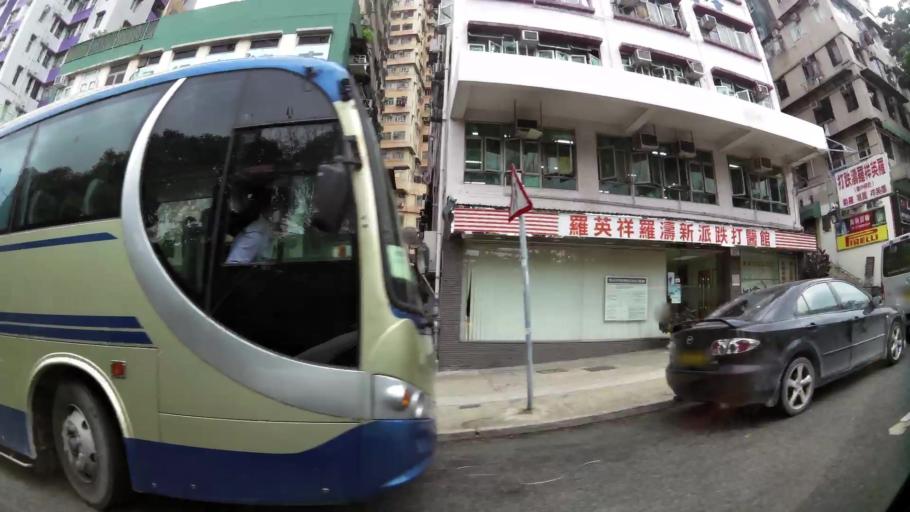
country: HK
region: Wong Tai Sin
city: Wong Tai Sin
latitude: 22.3464
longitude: 114.2026
